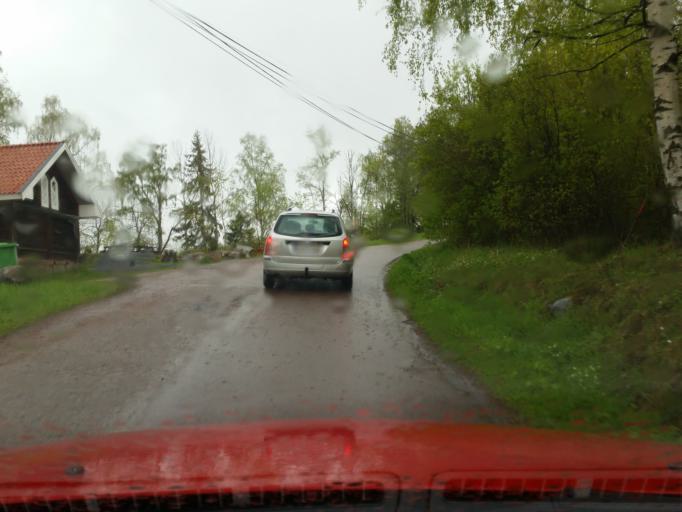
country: SE
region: Dalarna
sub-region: Saters Kommun
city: Saeter
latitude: 60.3602
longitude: 15.7891
